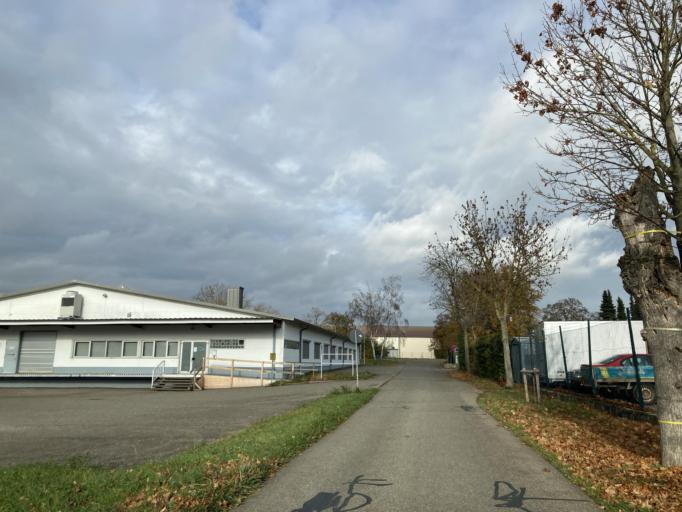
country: DE
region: Baden-Wuerttemberg
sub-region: Freiburg Region
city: Mullheim
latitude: 47.8087
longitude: 7.6046
